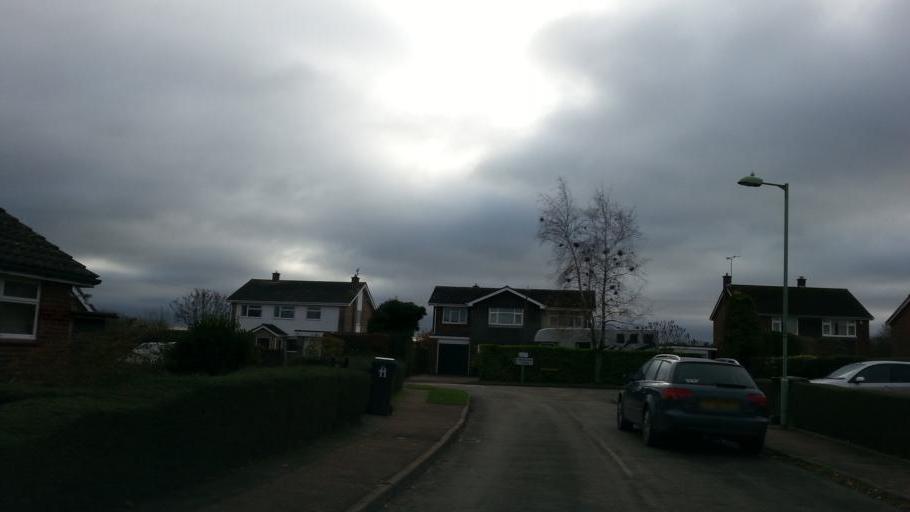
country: GB
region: England
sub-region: Suffolk
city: Framlingham
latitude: 52.3006
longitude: 1.3631
